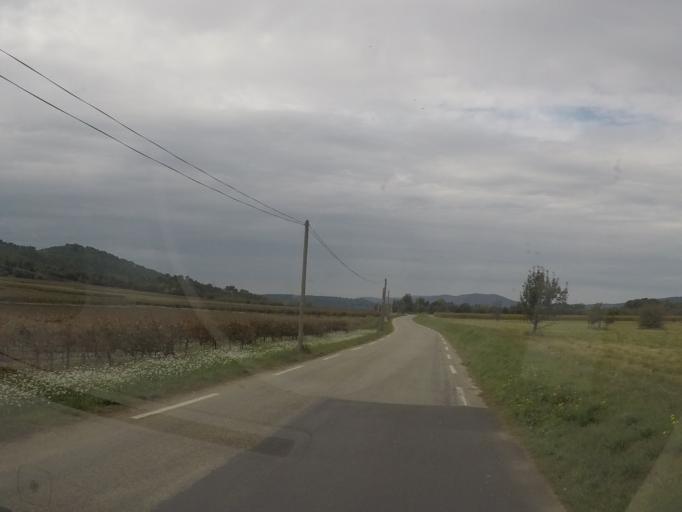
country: FR
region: Provence-Alpes-Cote d'Azur
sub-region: Departement du Vaucluse
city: Villelaure
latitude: 43.7430
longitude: 5.4286
